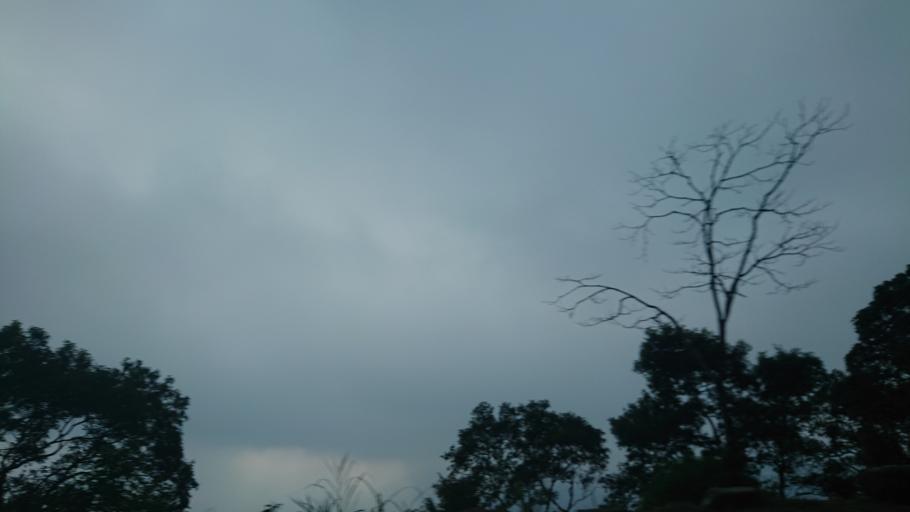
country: TW
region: Taiwan
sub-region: Chiayi
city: Jiayi Shi
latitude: 23.4650
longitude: 120.7186
